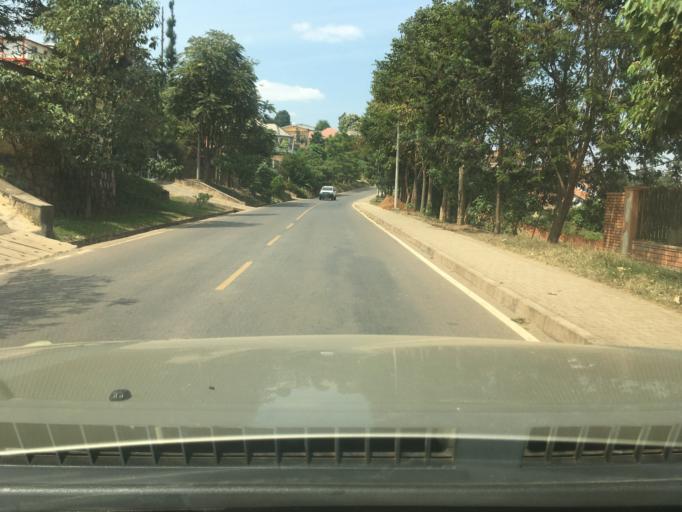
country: RW
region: Kigali
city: Kigali
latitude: -1.9561
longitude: 30.1024
